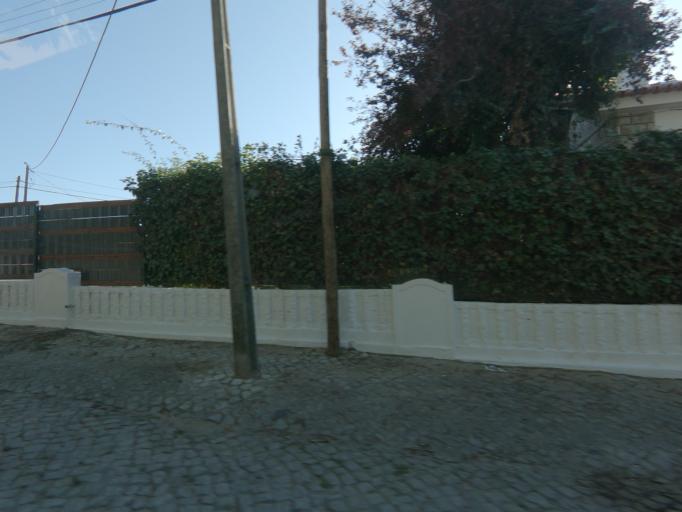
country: PT
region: Setubal
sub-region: Palmela
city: Palmela
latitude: 38.5756
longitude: -8.9068
